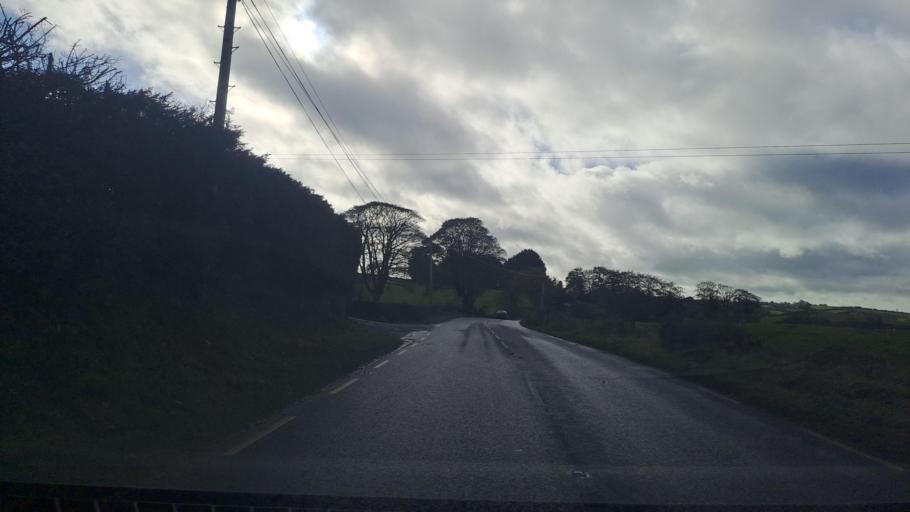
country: IE
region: Ulster
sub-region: County Monaghan
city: Monaghan
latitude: 54.2104
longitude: -6.9856
